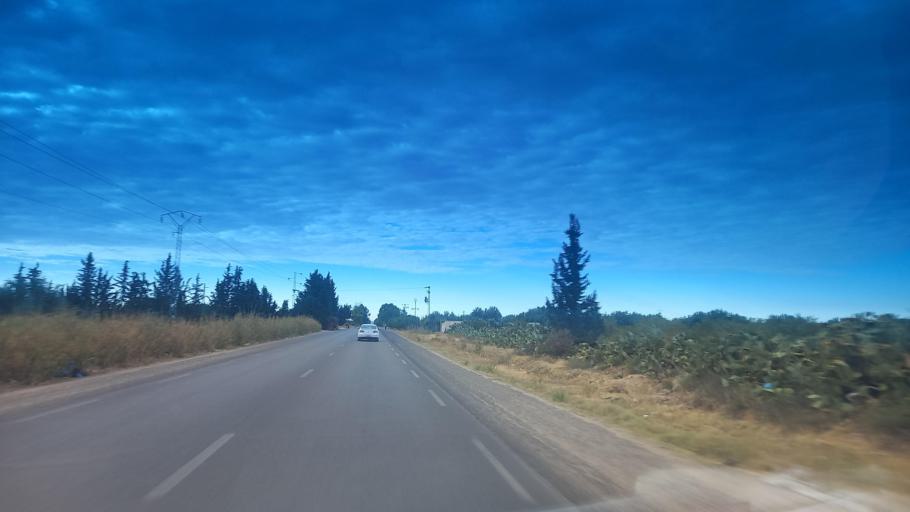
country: TN
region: Al Qasrayn
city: Sbiba
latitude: 35.3029
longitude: 9.0877
